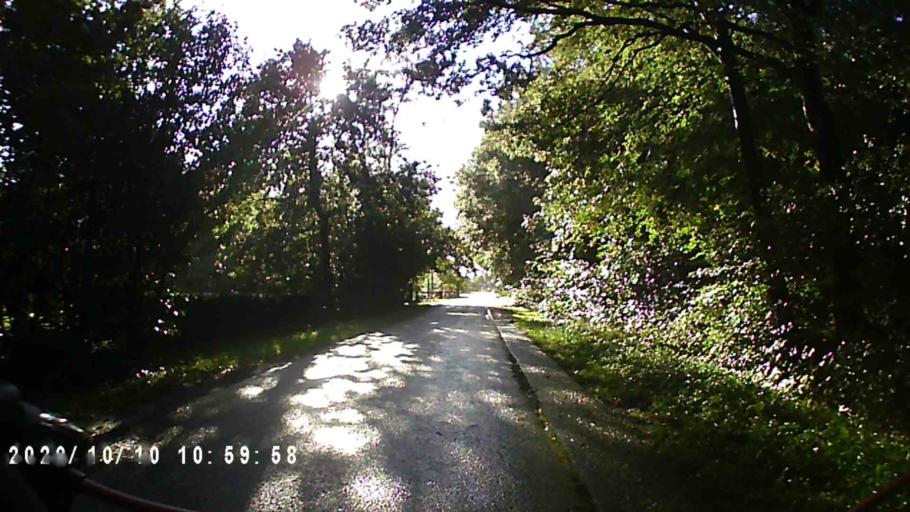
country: NL
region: Friesland
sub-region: Gemeente Achtkarspelen
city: Surhuisterveen
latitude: 53.1407
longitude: 6.2107
